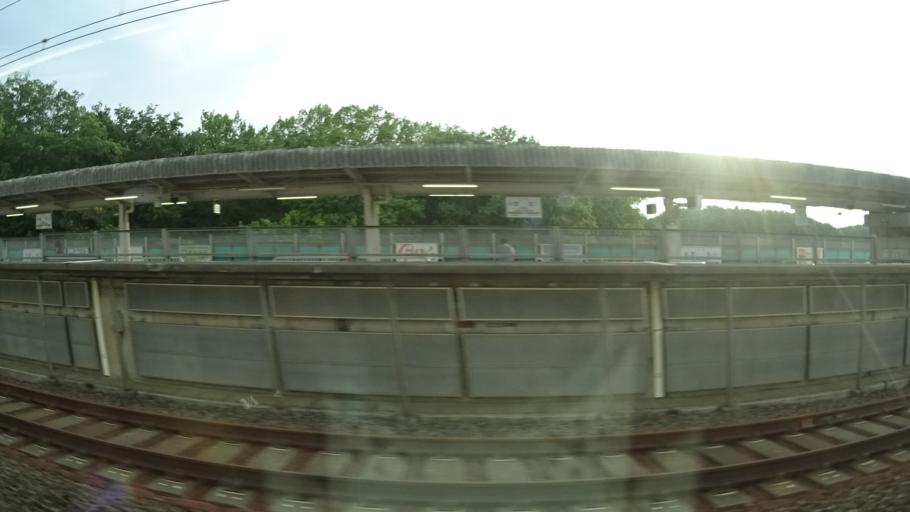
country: JP
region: Saitama
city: Ageoshimo
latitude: 35.9917
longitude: 139.6221
